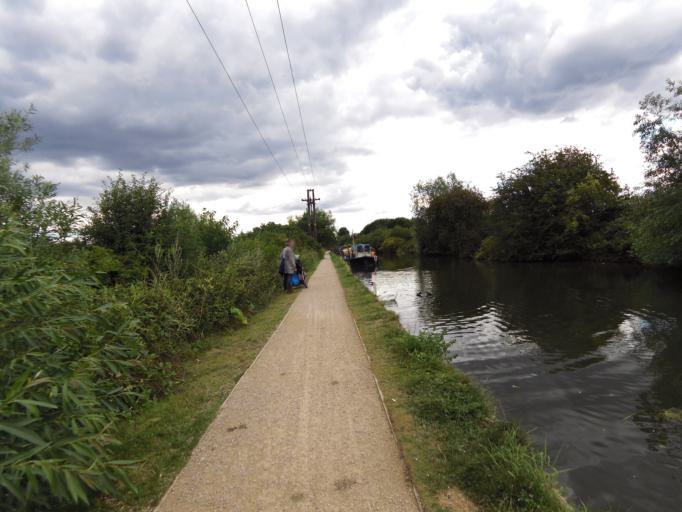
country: GB
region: England
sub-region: Hertfordshire
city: Cheshunt
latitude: 51.7046
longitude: -0.0192
